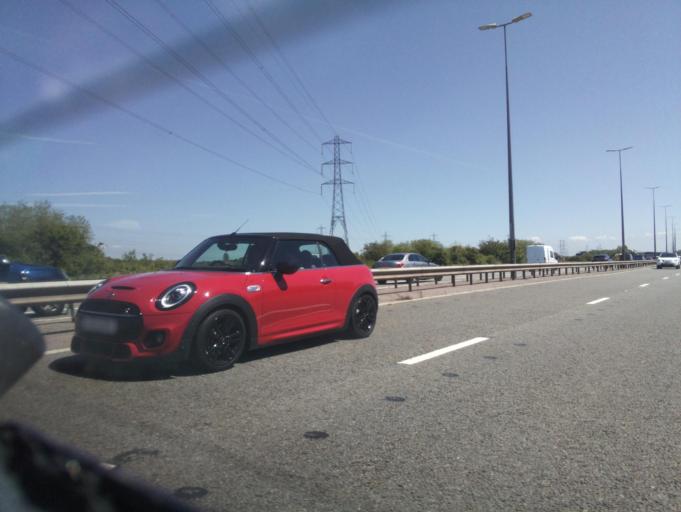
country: GB
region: Wales
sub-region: Monmouthshire
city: Caldicot
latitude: 51.5814
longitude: -2.7668
